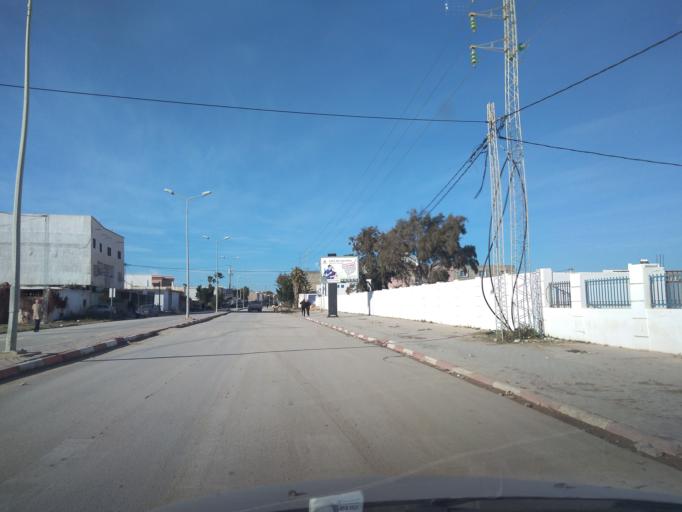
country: TN
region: Ariana
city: Qal'at al Andalus
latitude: 37.0537
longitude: 10.1218
